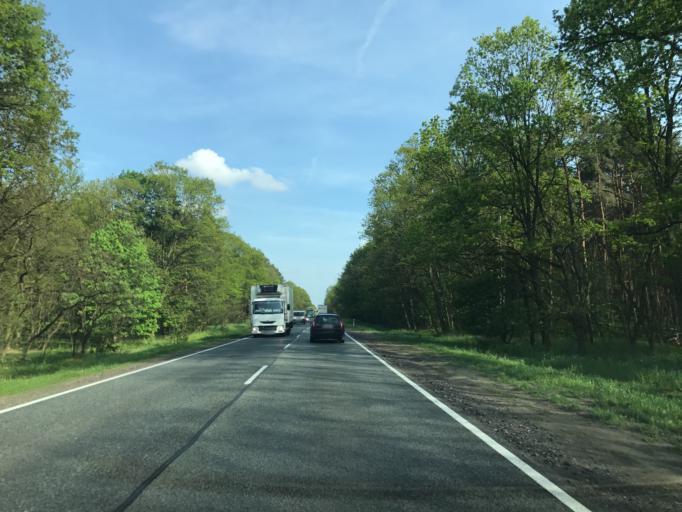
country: PL
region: Kujawsko-Pomorskie
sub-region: Powiat torunski
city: Zlawies Wielka
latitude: 53.0450
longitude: 18.3813
